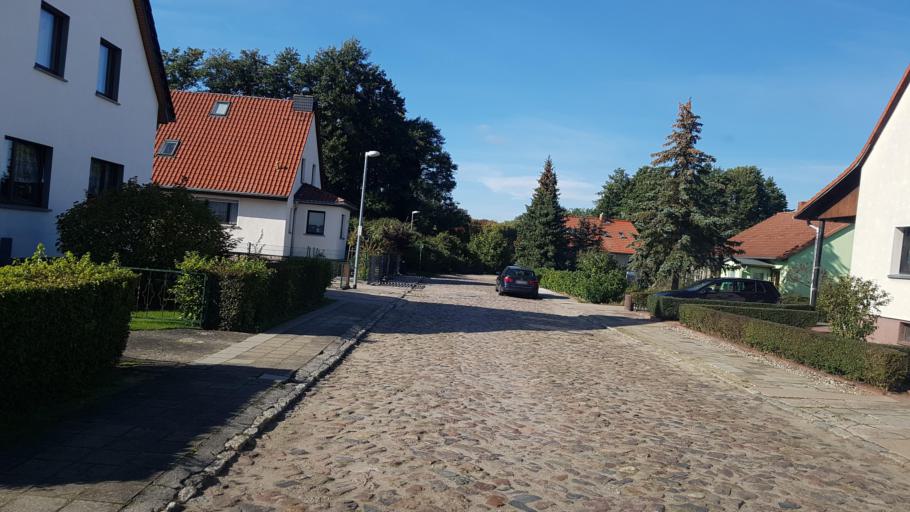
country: DE
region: Brandenburg
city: Belzig
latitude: 52.1450
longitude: 12.6012
